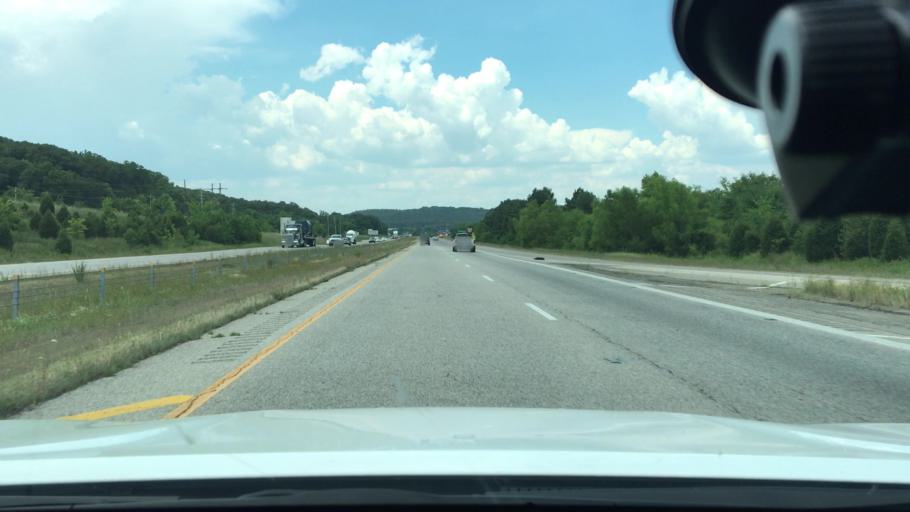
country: US
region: Arkansas
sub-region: Washington County
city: Fayetteville
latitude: 36.0393
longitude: -94.1894
